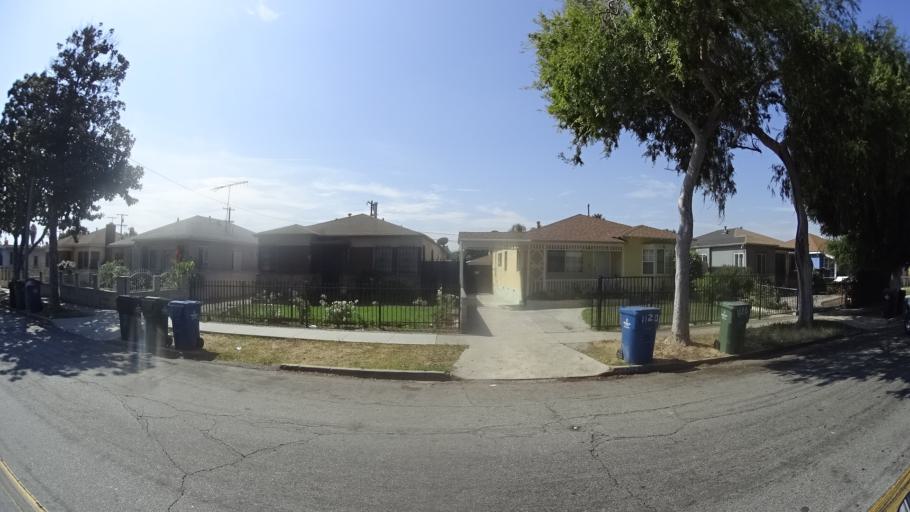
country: US
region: California
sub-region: Los Angeles County
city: View Park-Windsor Hills
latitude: 33.9805
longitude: -118.3374
